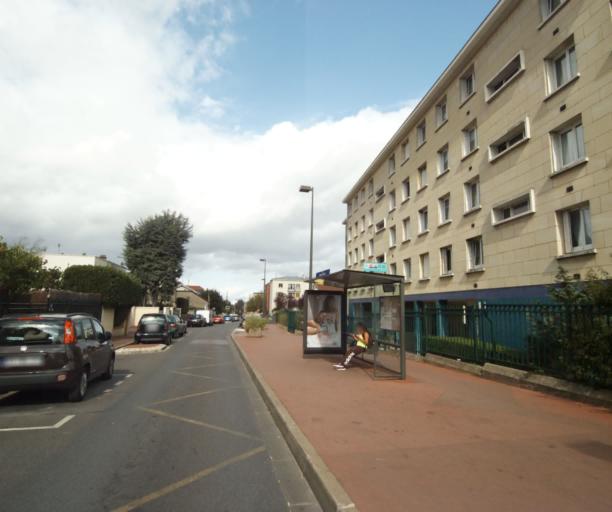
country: FR
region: Ile-de-France
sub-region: Departement des Hauts-de-Seine
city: Clamart
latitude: 48.8079
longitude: 2.2776
